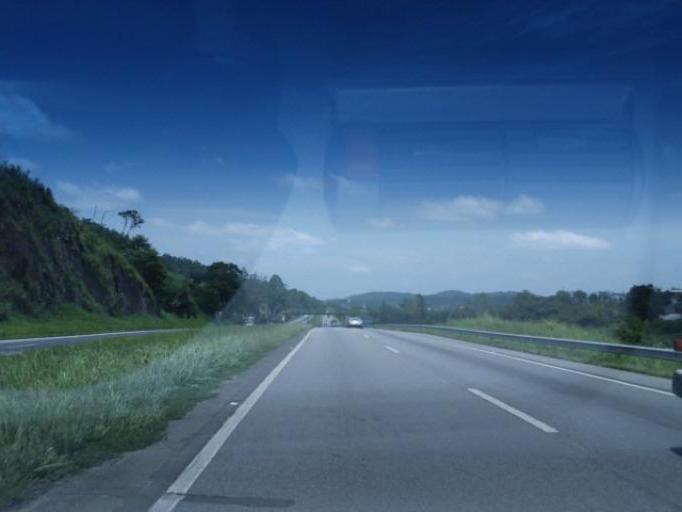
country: BR
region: Sao Paulo
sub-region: Miracatu
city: Miracatu
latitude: -24.2851
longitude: -47.4404
